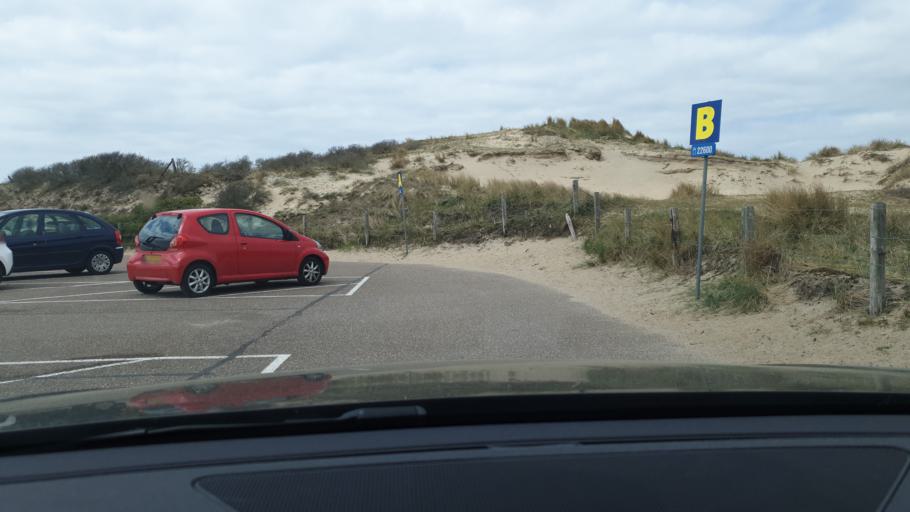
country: NL
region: South Holland
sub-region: Gemeente Noordwijkerhout
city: Noordwijkerhout
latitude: 52.3010
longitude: 4.4799
